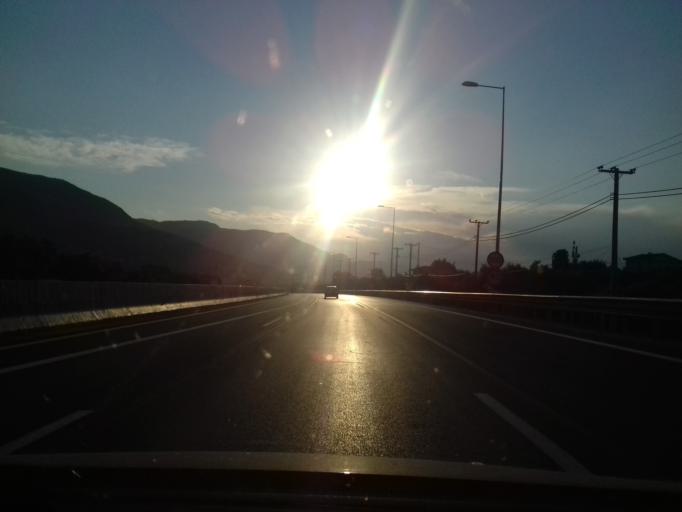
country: GR
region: West Greece
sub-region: Nomos Achaias
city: Akrata
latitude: 38.1714
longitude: 22.2935
